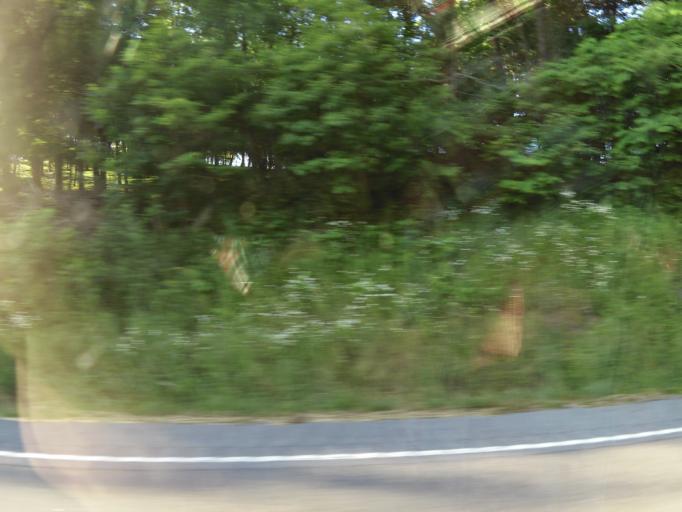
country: US
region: Tennessee
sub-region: Sevier County
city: Sevierville
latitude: 35.8527
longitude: -83.6381
